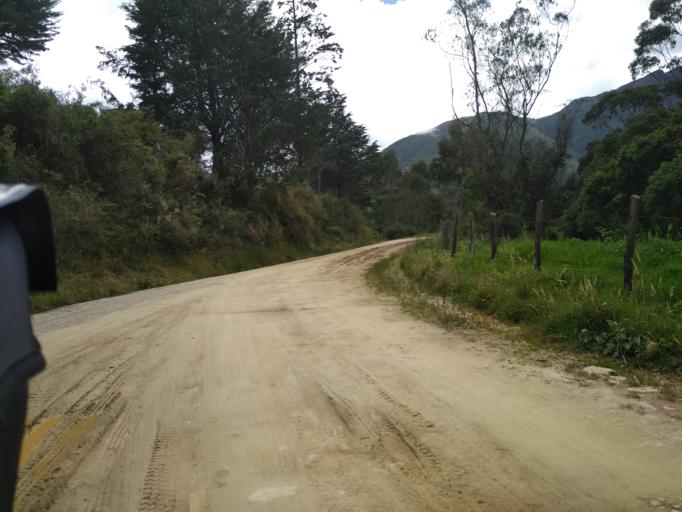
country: CO
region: Boyaca
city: Duitama
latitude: 5.9417
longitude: -73.1303
